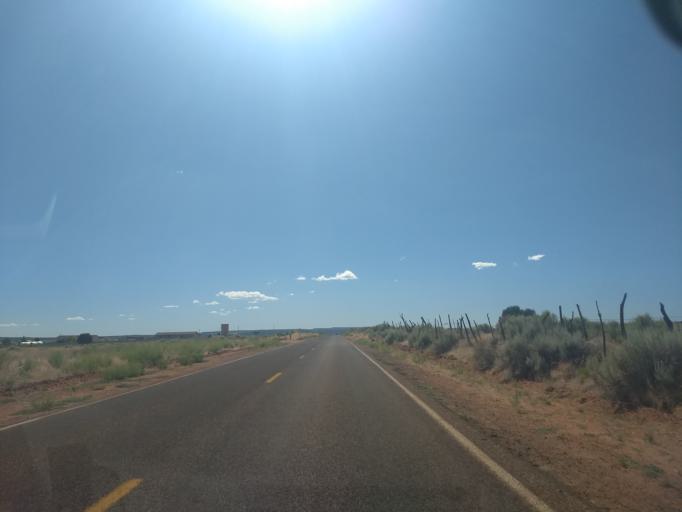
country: US
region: Arizona
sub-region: Mohave County
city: Colorado City
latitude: 36.9469
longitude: -112.9322
